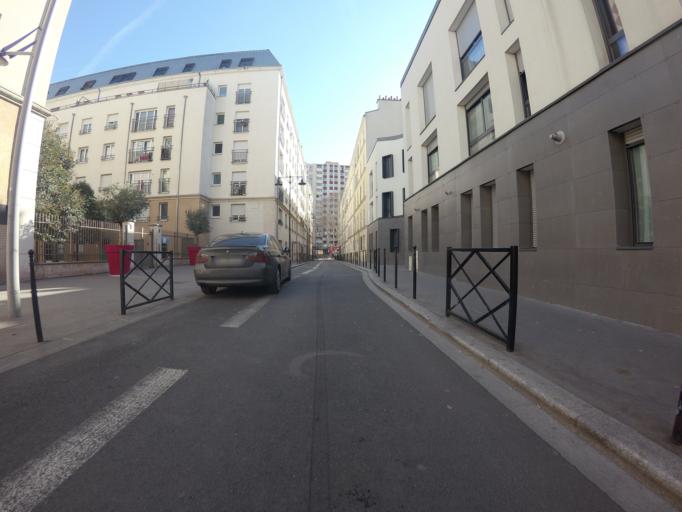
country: FR
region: Ile-de-France
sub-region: Departement des Hauts-de-Seine
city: Clichy
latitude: 48.9000
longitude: 2.3124
